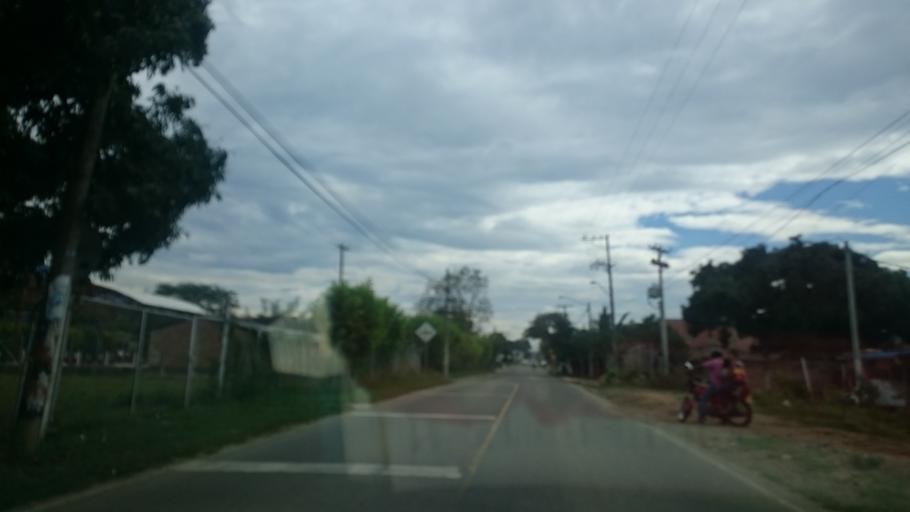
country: CO
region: Cauca
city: Santander de Quilichao
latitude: 3.0224
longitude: -76.4785
